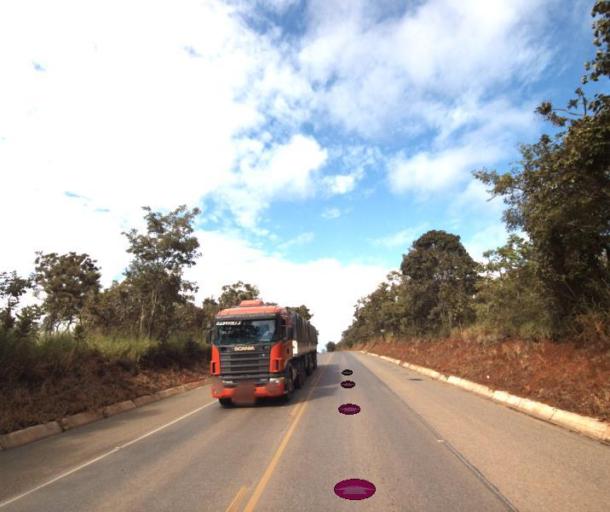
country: BR
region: Goias
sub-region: Uruacu
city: Uruacu
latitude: -14.7435
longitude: -49.2485
